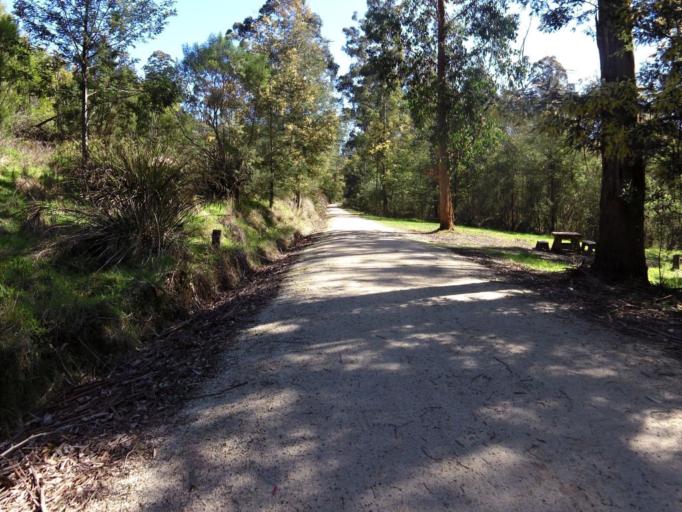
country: AU
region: Victoria
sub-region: Latrobe
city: Moe
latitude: -38.3847
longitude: 146.2495
